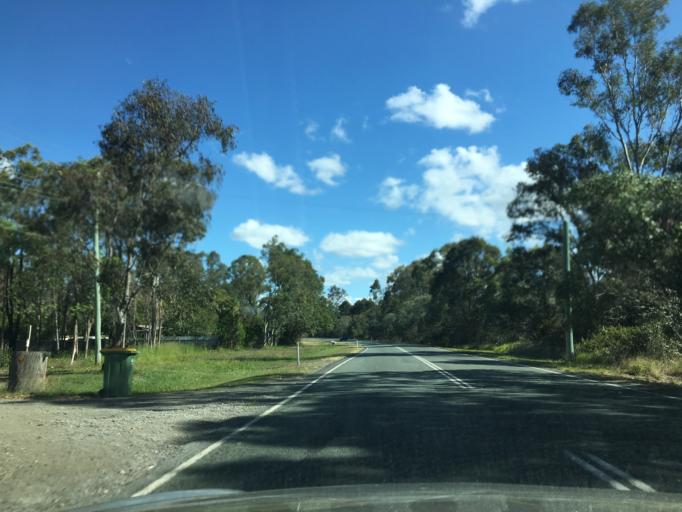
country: AU
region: Queensland
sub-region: Logan
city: Waterford West
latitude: -27.7245
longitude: 153.1274
